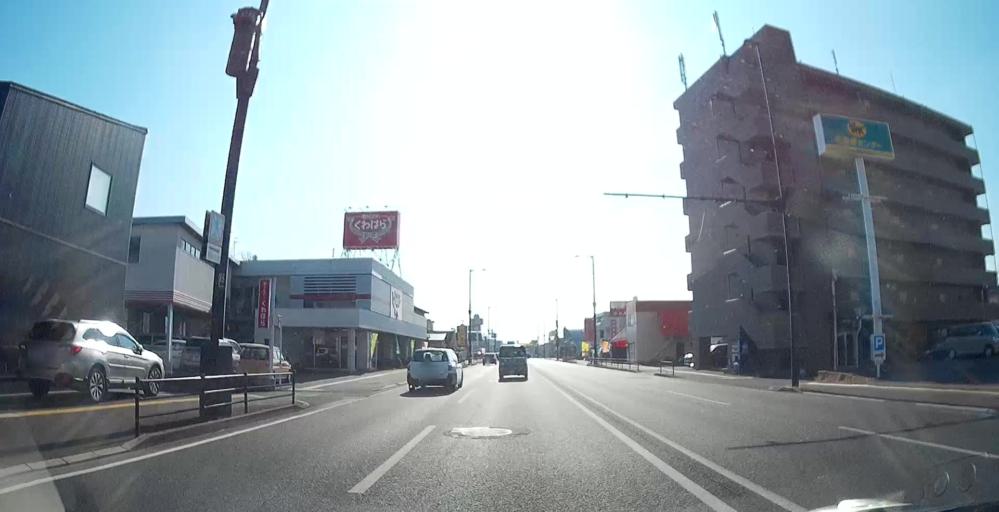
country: JP
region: Kumamoto
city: Kumamoto
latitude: 32.7684
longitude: 130.6924
